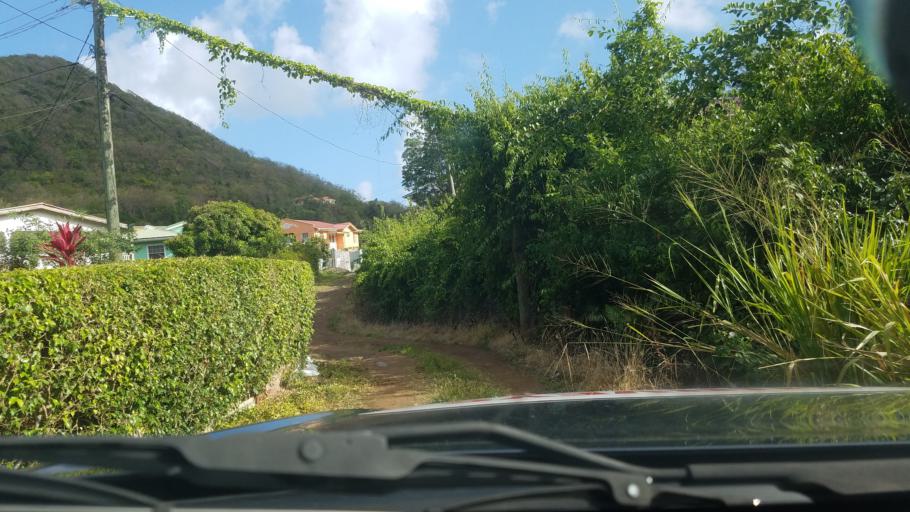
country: LC
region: Gros-Islet
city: Gros Islet
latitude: 14.0641
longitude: -60.9573
